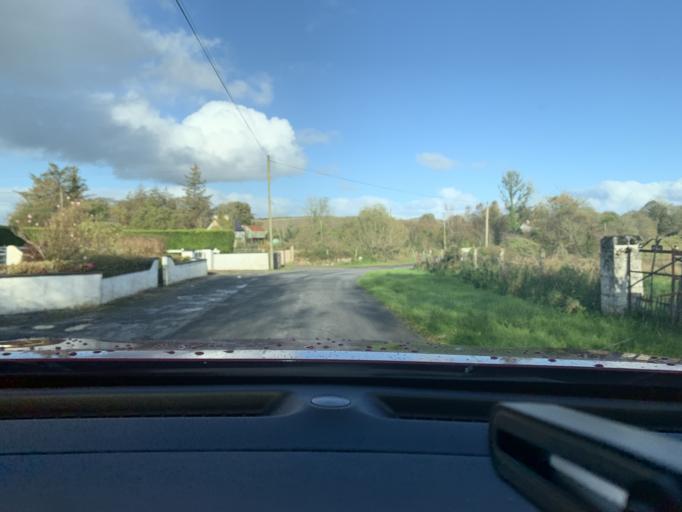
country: IE
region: Connaught
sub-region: Sligo
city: Ballymote
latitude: 54.1080
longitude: -8.4328
